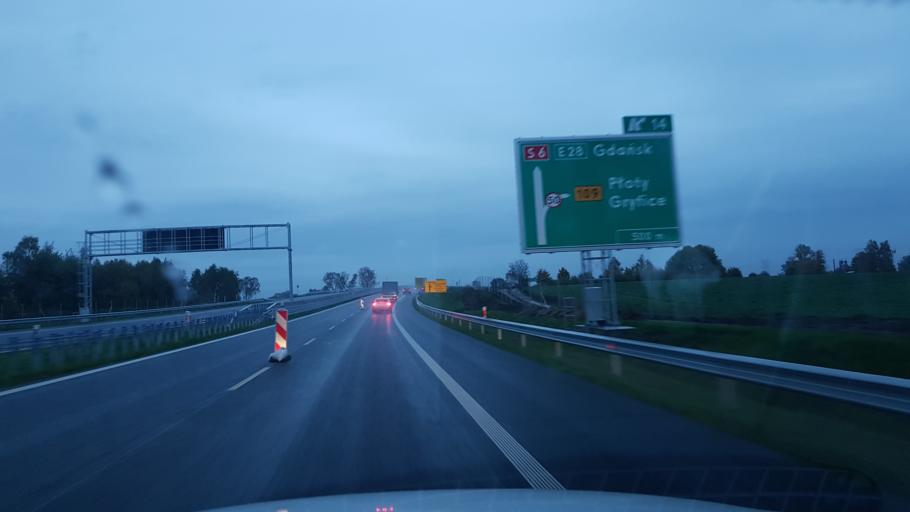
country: PL
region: West Pomeranian Voivodeship
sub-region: Powiat gryficki
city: Ploty
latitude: 53.8102
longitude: 15.2477
